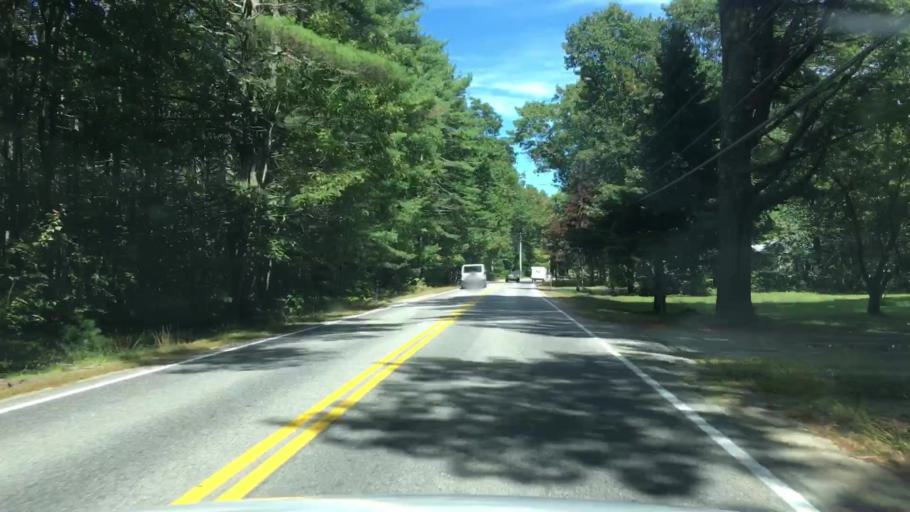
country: US
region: Maine
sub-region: Cumberland County
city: West Scarborough
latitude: 43.5969
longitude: -70.4285
